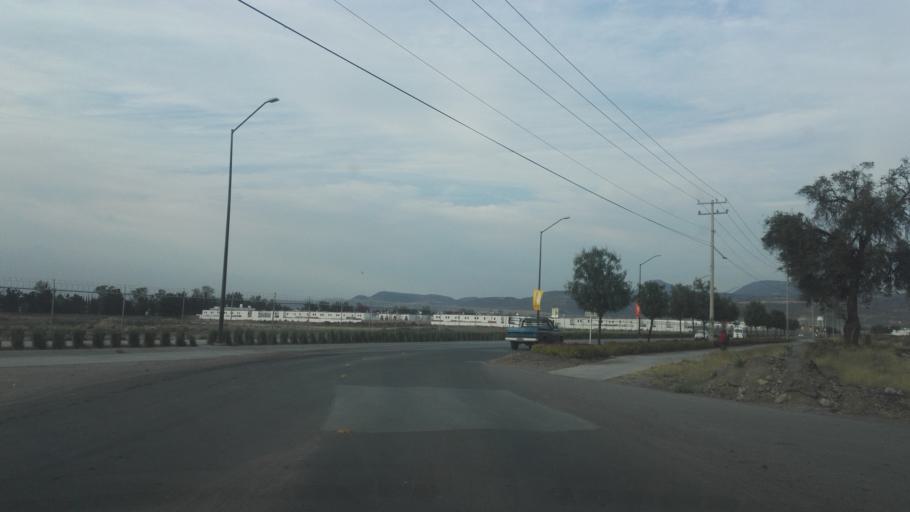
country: MX
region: Guanajuato
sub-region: Leon
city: Fraccionamiento Paraiso Real
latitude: 21.0804
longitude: -101.6018
